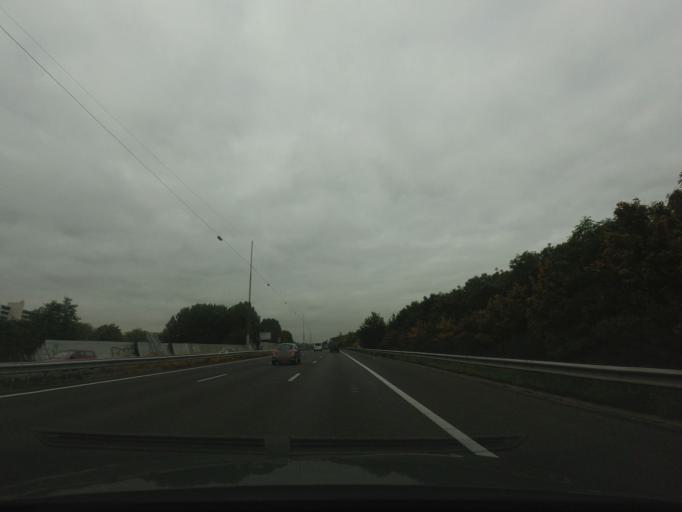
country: NL
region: North Holland
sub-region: Gemeente Landsmeer
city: Landsmeer
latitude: 52.4006
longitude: 4.9558
